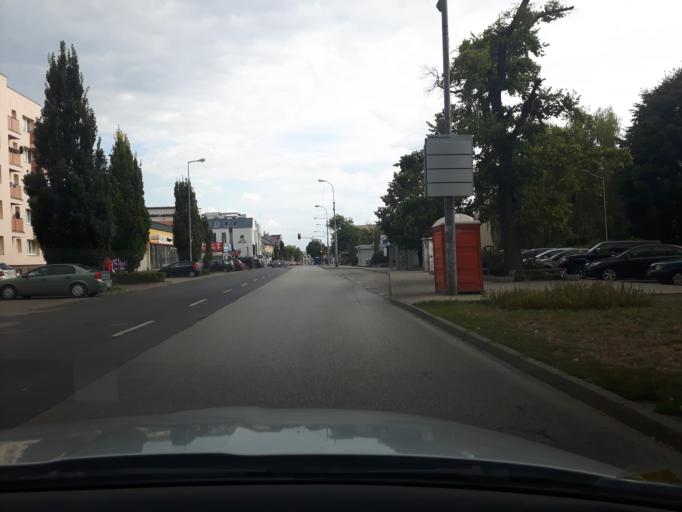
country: PL
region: Masovian Voivodeship
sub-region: Powiat piaseczynski
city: Piaseczno
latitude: 52.0788
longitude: 21.0249
